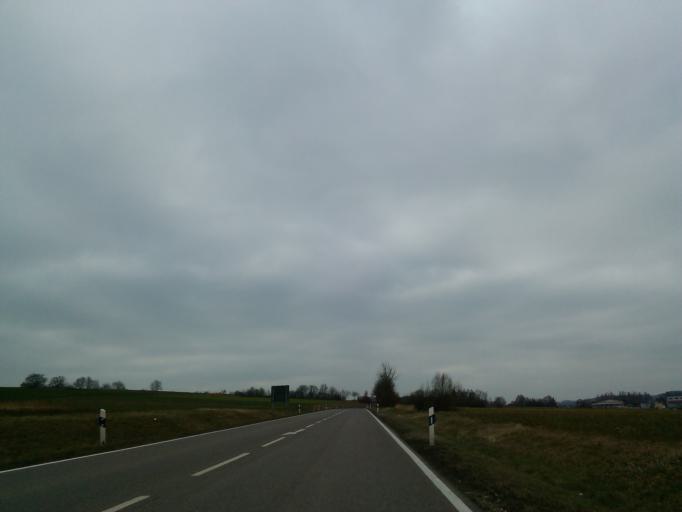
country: DE
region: Bavaria
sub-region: Swabia
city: Ziemetshausen
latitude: 48.2935
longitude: 10.5482
